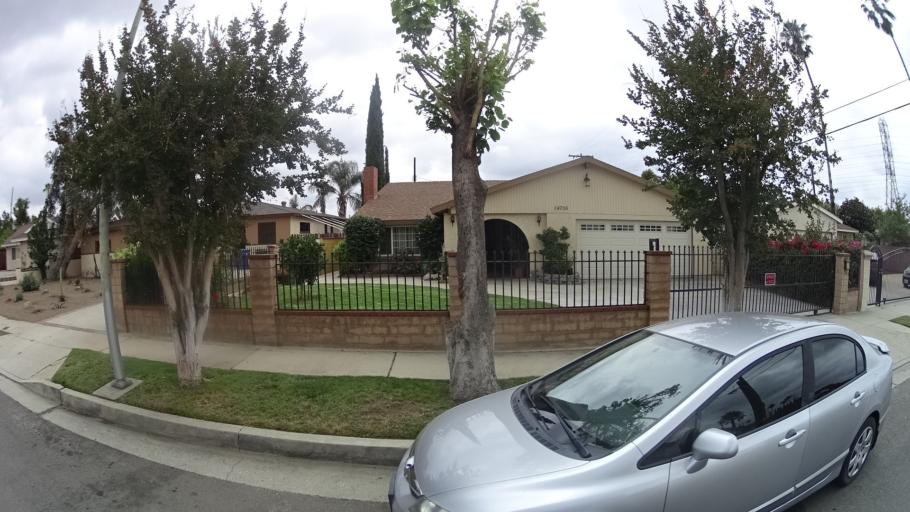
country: US
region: California
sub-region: Los Angeles County
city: San Fernando
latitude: 34.2618
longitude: -118.4524
